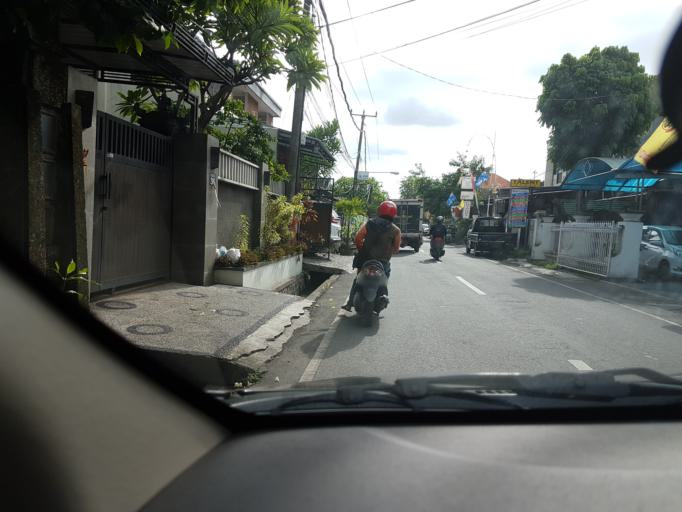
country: ID
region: Bali
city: Denpasar
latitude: -8.6645
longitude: 115.1964
